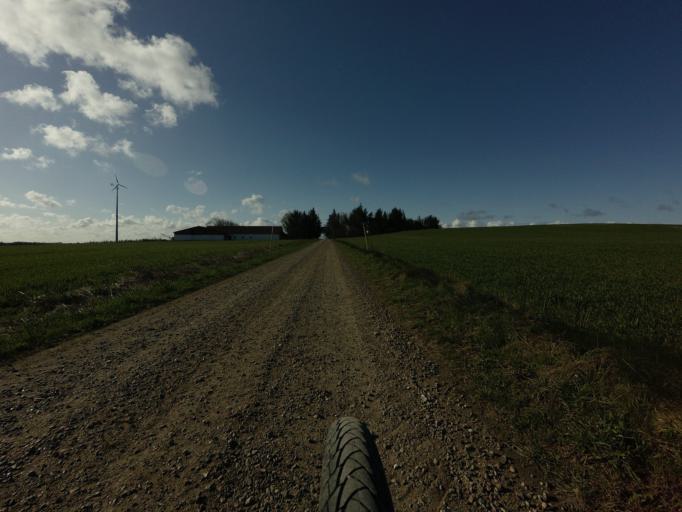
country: DK
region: North Denmark
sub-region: Hjorring Kommune
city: Vra
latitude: 57.3655
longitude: 9.8167
